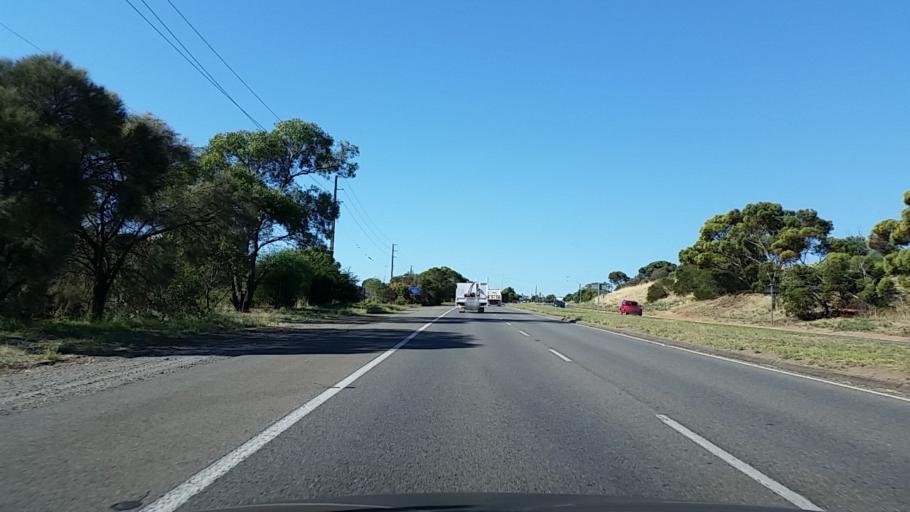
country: AU
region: South Australia
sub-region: Adelaide
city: Port Noarlunga
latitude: -35.1228
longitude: 138.4874
